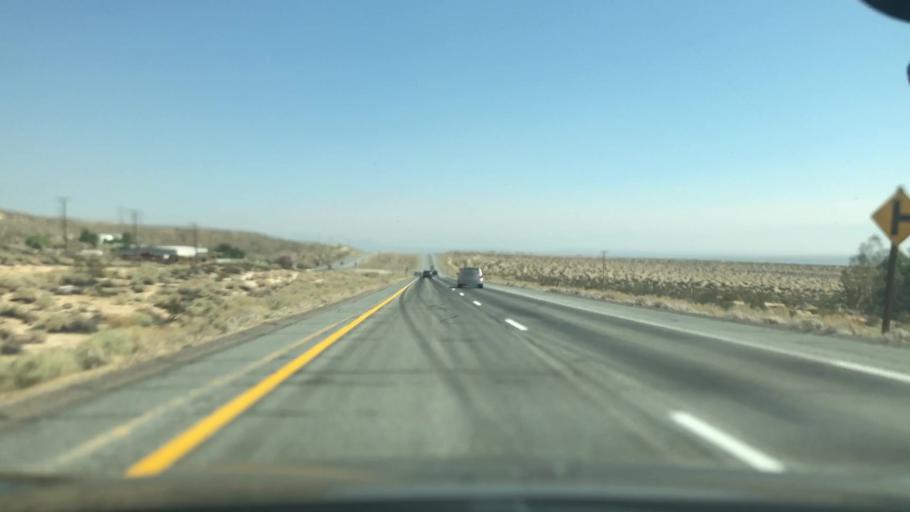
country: US
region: California
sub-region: Kern County
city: Inyokern
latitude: 35.6646
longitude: -117.8728
